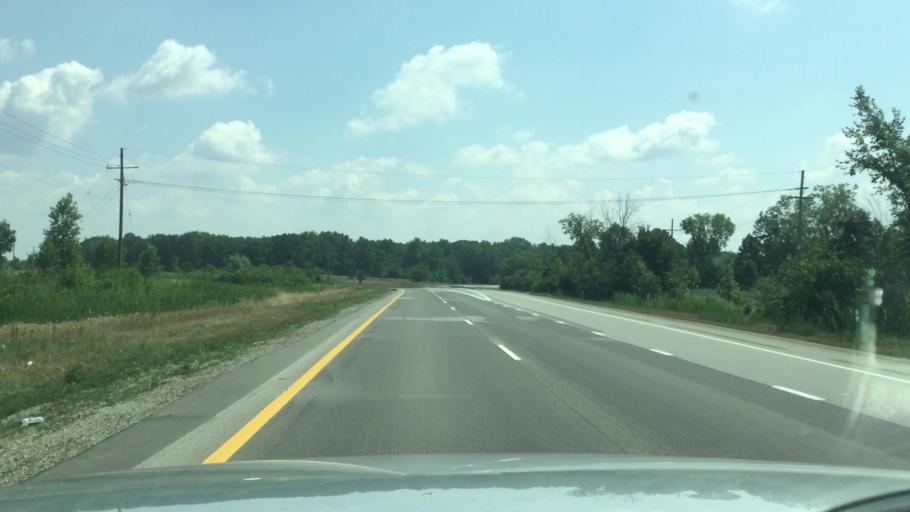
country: US
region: Michigan
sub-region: Washtenaw County
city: Ypsilanti
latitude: 42.2482
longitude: -83.5486
